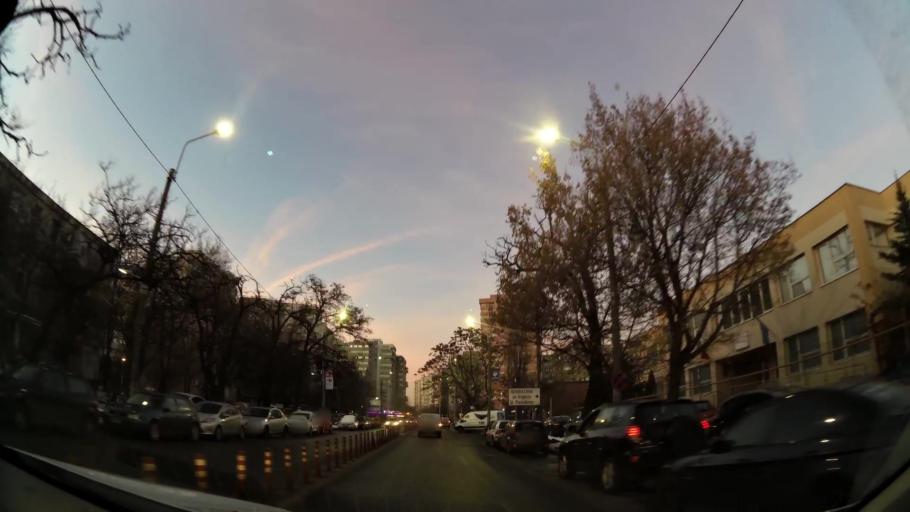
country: RO
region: Ilfov
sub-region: Comuna Fundeni-Dobroesti
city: Fundeni
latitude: 44.4416
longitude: 26.1505
